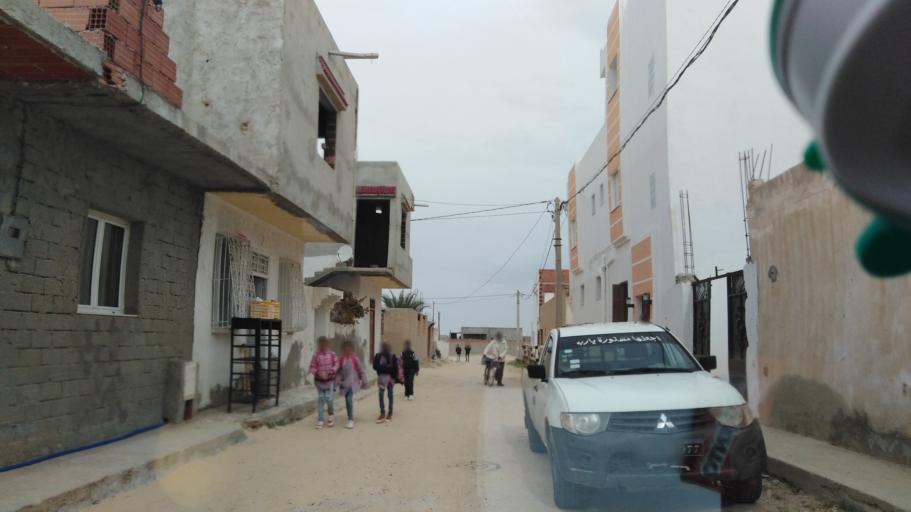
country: TN
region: Qabis
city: Gabes
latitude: 33.9520
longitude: 10.0038
